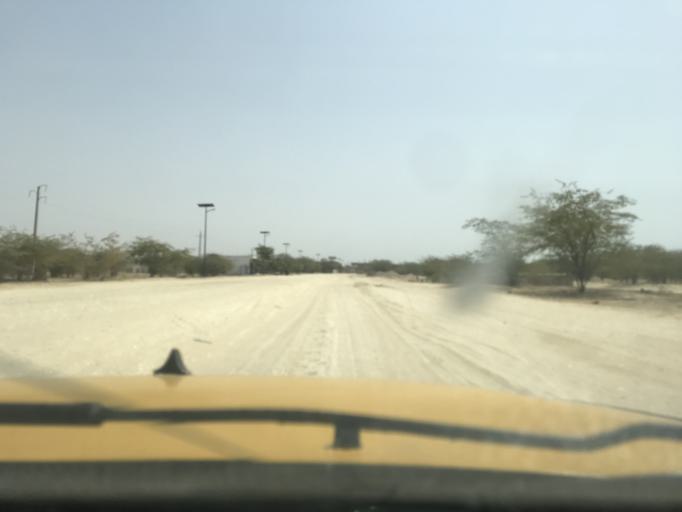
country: SN
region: Saint-Louis
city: Saint-Louis
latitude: 16.0235
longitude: -16.4462
